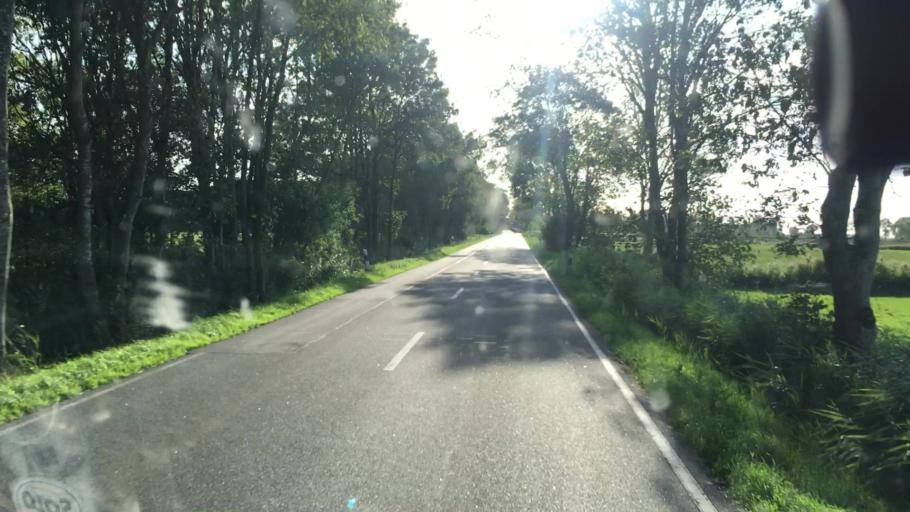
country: DE
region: Lower Saxony
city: Wittmund
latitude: 53.6418
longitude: 7.7982
